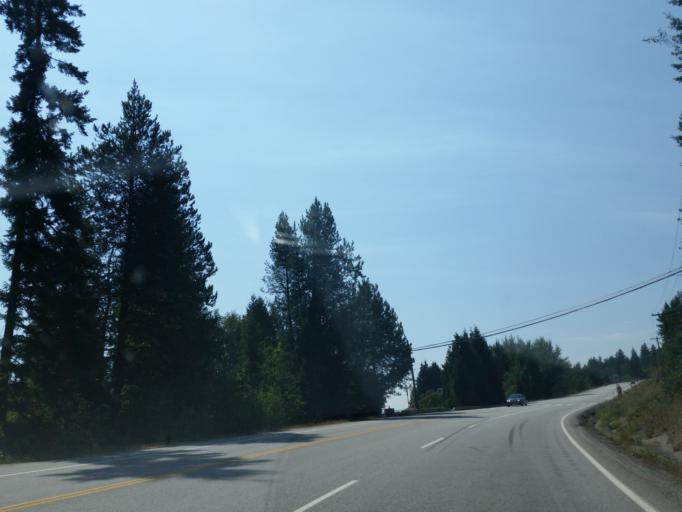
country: CA
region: British Columbia
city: Castlegar
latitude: 49.2938
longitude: -117.6562
